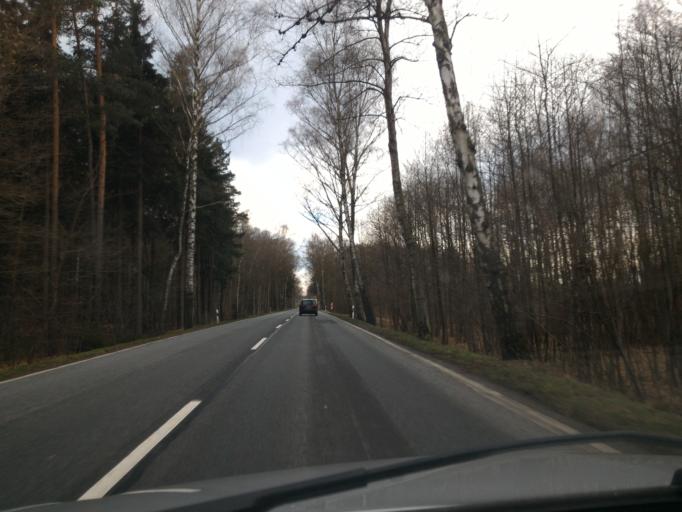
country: DE
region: Saxony
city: Stolpen
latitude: 51.0846
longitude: 14.0518
